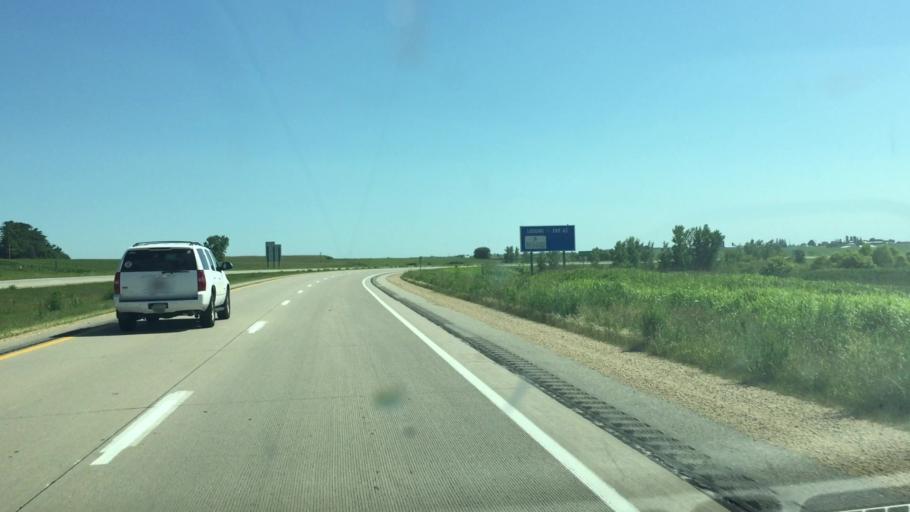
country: US
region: Iowa
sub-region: Jones County
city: Monticello
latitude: 42.2132
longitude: -91.1741
